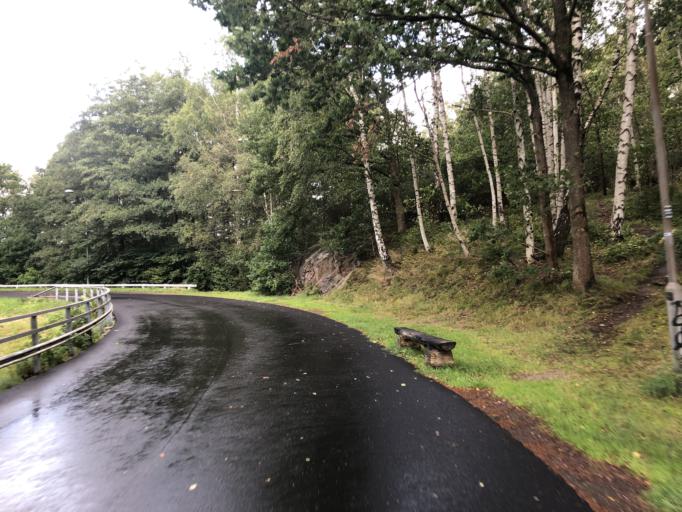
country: SE
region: Vaestra Goetaland
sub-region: Goteborg
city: Goeteborg
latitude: 57.7563
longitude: 11.9333
